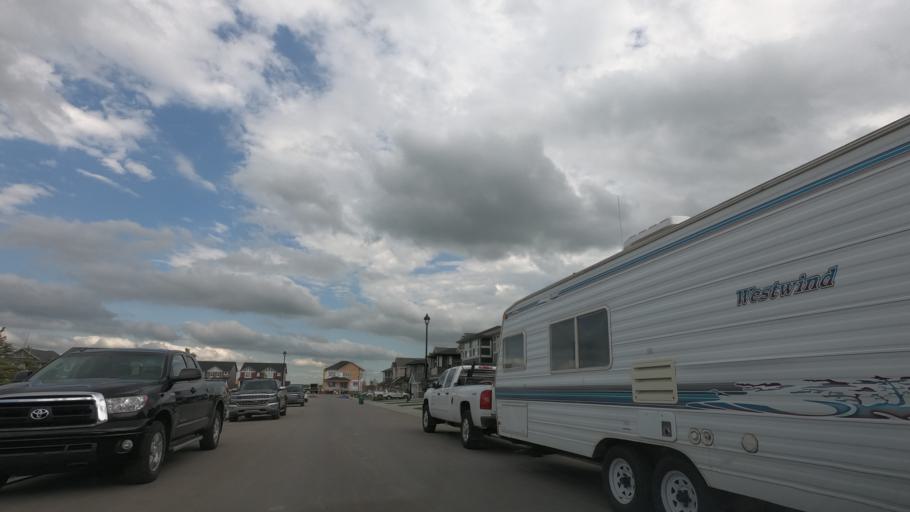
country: CA
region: Alberta
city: Airdrie
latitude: 51.2568
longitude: -113.9850
